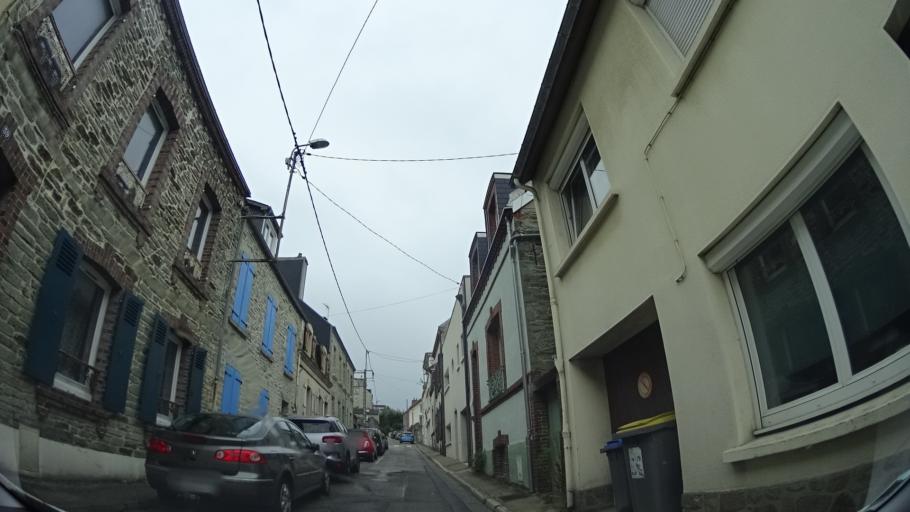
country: FR
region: Lower Normandy
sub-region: Departement de la Manche
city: Cherbourg-Octeville
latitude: 49.6322
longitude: -1.6273
